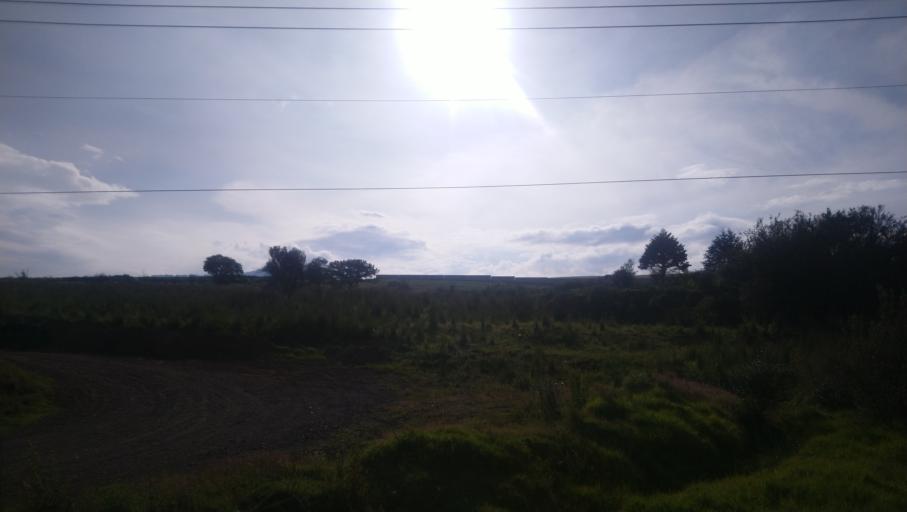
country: MX
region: Mexico
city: Juchitepec de Mariano Riva Palacio
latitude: 19.1219
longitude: -98.9374
